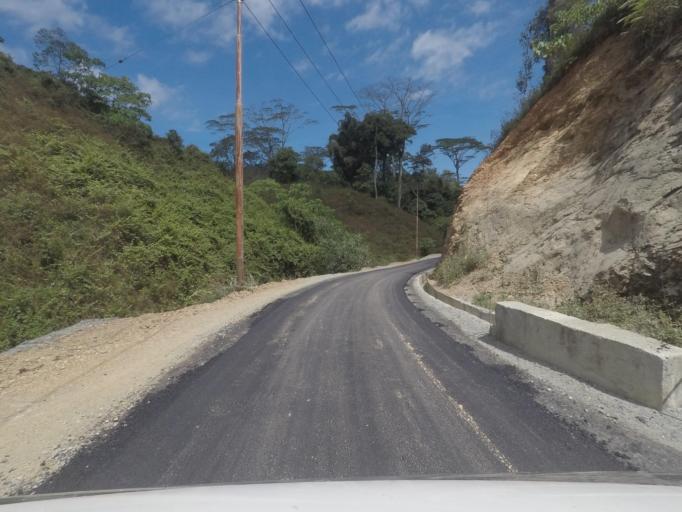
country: TL
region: Ermera
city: Gleno
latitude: -8.7524
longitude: 125.3386
